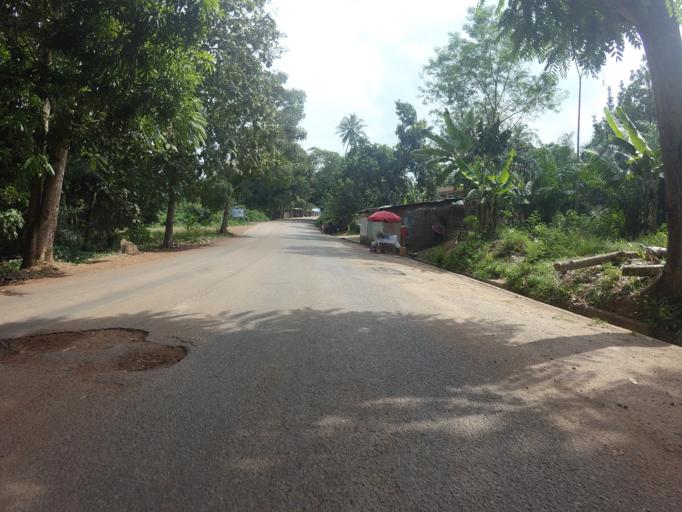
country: GH
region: Eastern
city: Aburi
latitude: 5.9521
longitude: -0.2123
